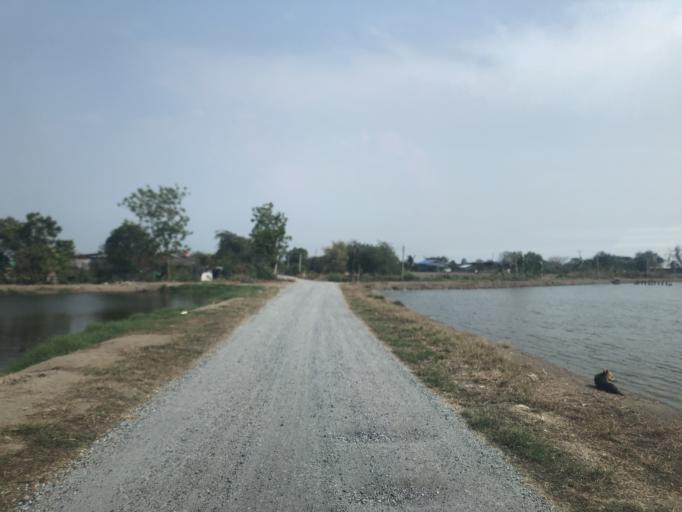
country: TH
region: Chachoengsao
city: Bang Pakong
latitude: 13.5155
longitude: 100.9207
